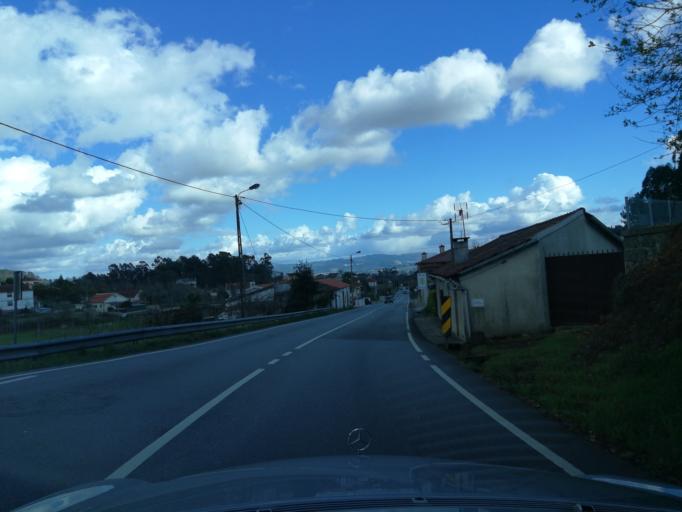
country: PT
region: Braga
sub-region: Vila Verde
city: Prado
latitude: 41.6494
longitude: -8.4998
